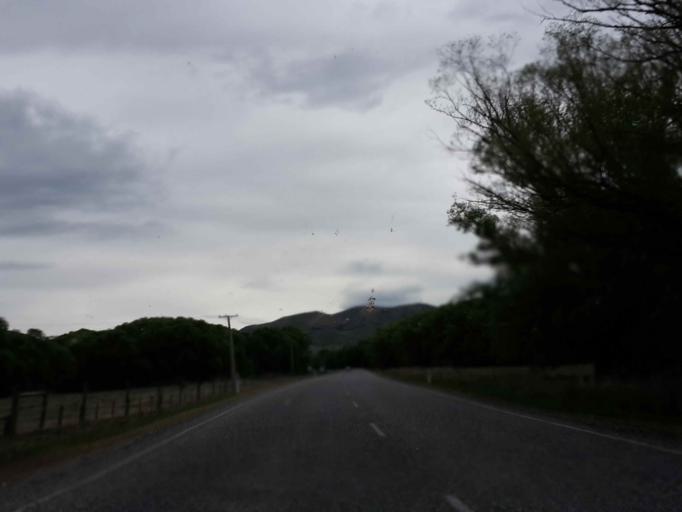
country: NZ
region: Otago
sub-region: Queenstown-Lakes District
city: Wanaka
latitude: -44.7801
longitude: 169.5073
